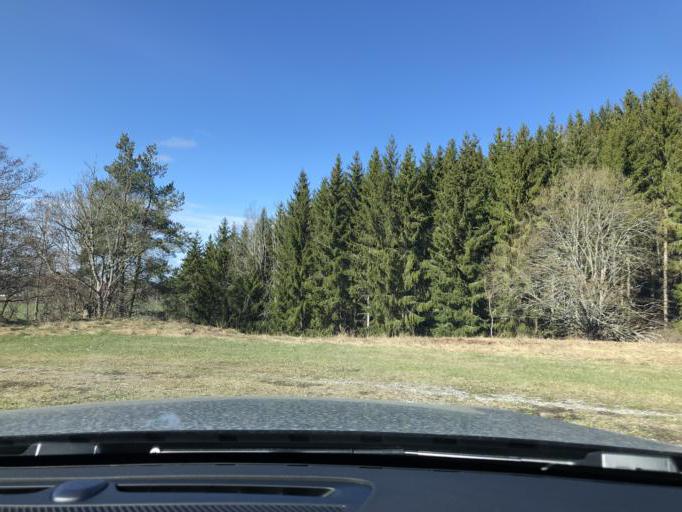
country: SE
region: Soedermanland
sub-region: Trosa Kommun
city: Vagnharad
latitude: 58.9344
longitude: 17.5258
